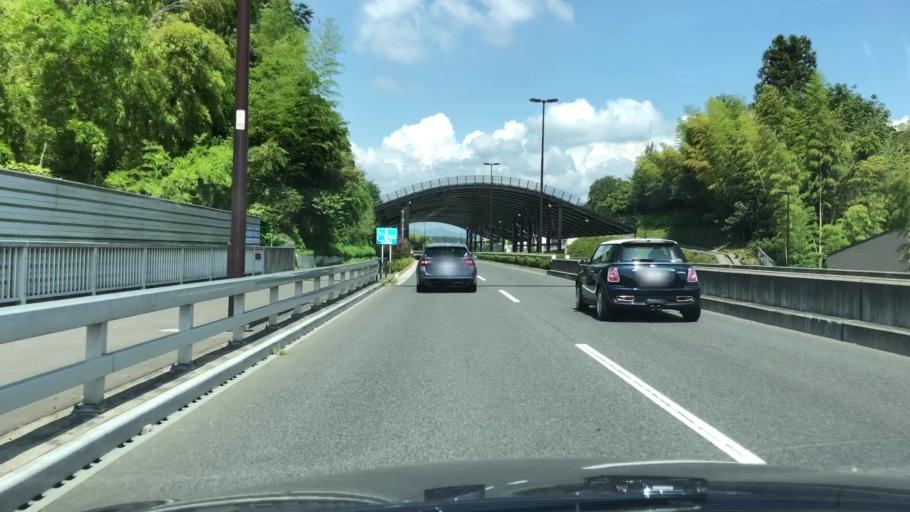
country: JP
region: Tokyo
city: Fussa
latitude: 35.7009
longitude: 139.3104
